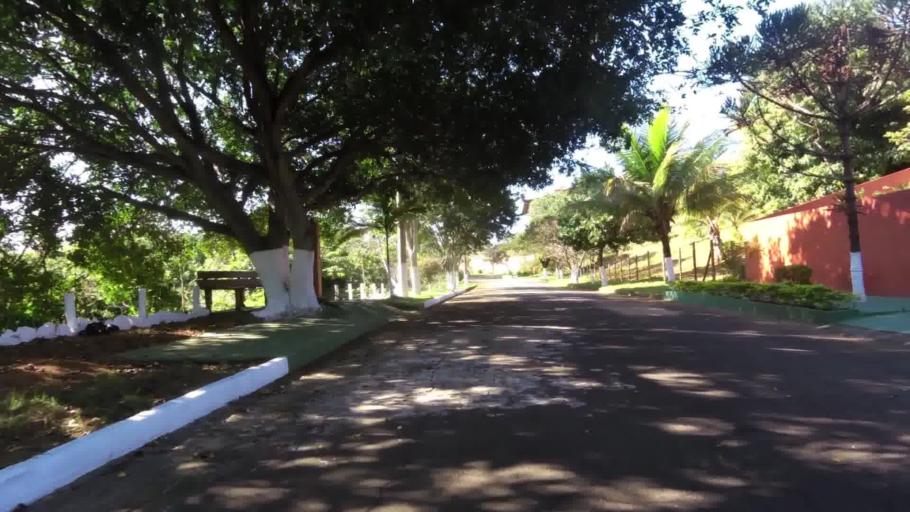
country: BR
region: Espirito Santo
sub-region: Guarapari
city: Guarapari
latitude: -20.7409
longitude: -40.5600
